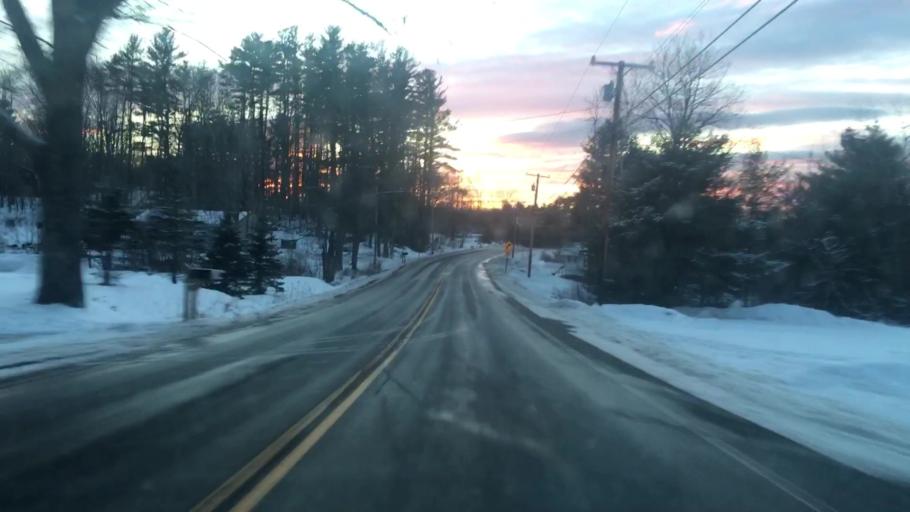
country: US
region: Maine
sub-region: Kennebec County
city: Pittston
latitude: 44.2210
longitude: -69.7409
